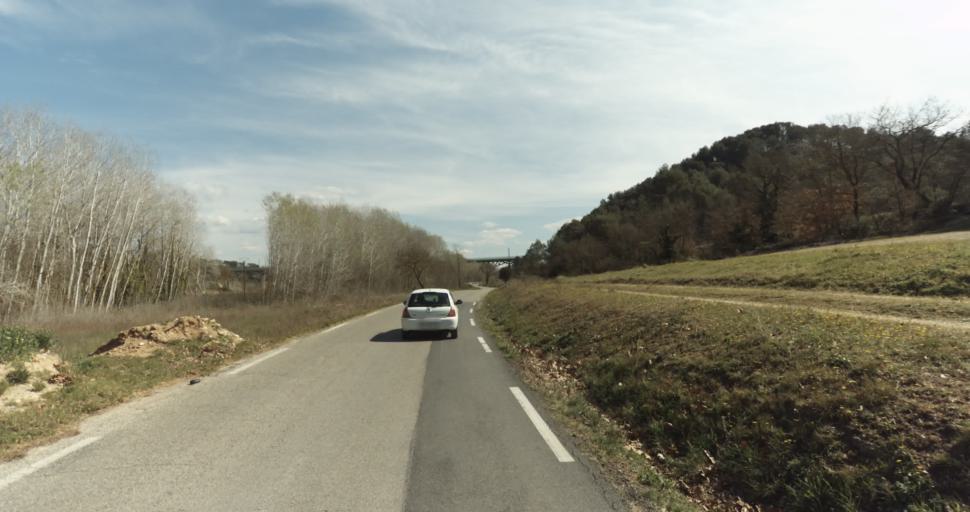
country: FR
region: Provence-Alpes-Cote d'Azur
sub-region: Departement des Bouches-du-Rhone
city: Ventabren
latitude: 43.5142
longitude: 5.3195
